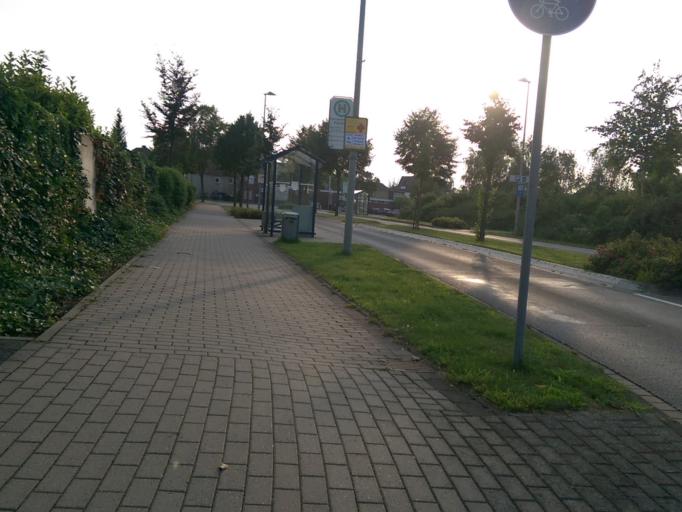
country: DE
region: North Rhine-Westphalia
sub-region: Regierungsbezirk Detmold
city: Rheda-Wiedenbruck
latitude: 51.8873
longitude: 8.2502
